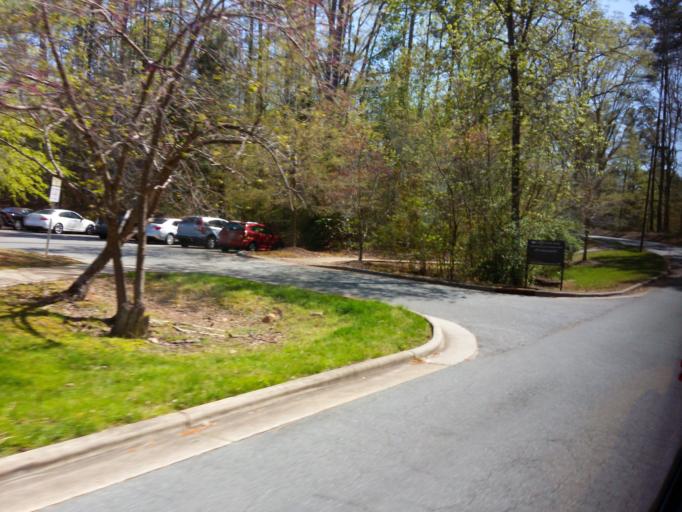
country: US
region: North Carolina
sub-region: Orange County
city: Chapel Hill
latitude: 35.9503
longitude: -79.0640
